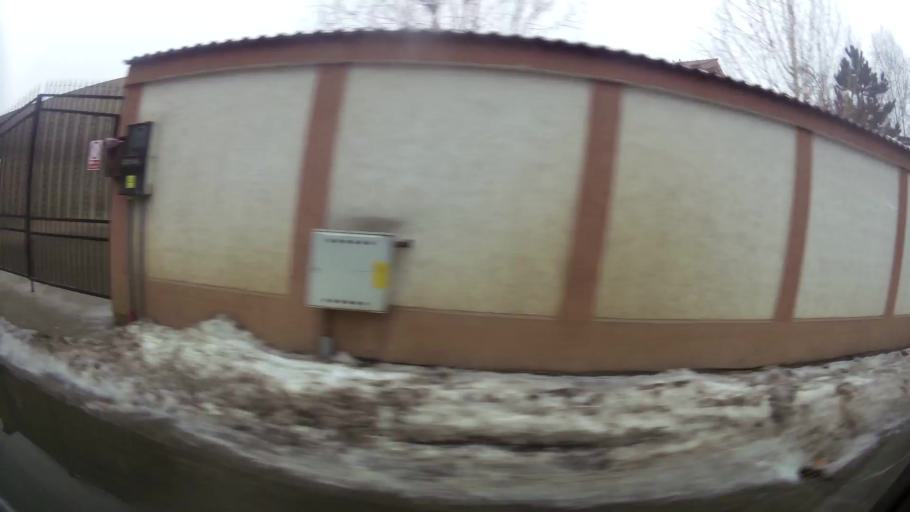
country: RO
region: Ilfov
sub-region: Comuna Chiajna
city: Rosu
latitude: 44.4550
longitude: 25.9949
